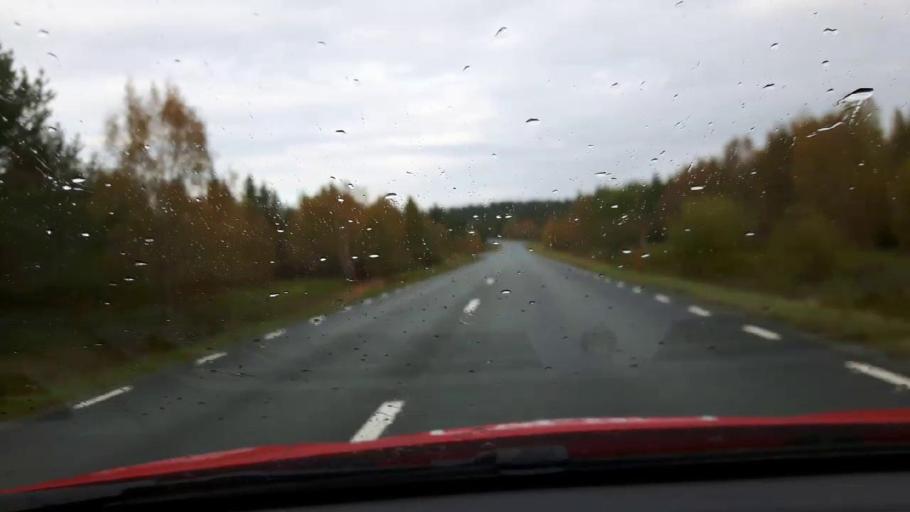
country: SE
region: Jaemtland
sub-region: Krokoms Kommun
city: Krokom
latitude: 63.0903
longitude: 14.2998
